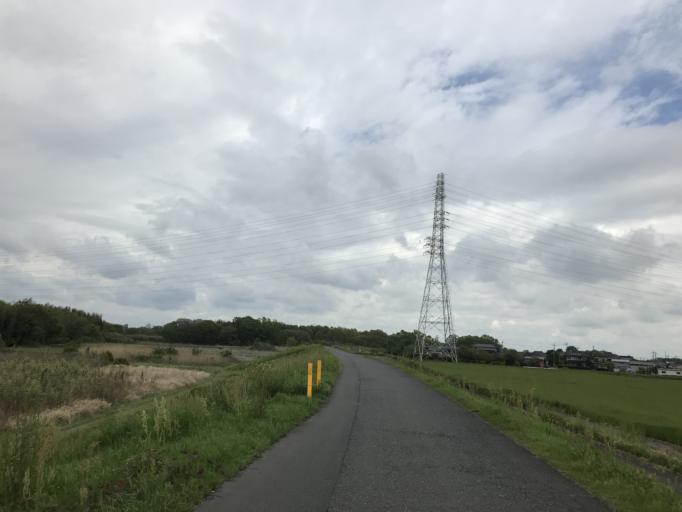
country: JP
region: Ibaraki
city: Mitsukaido
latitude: 36.0082
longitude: 139.9961
